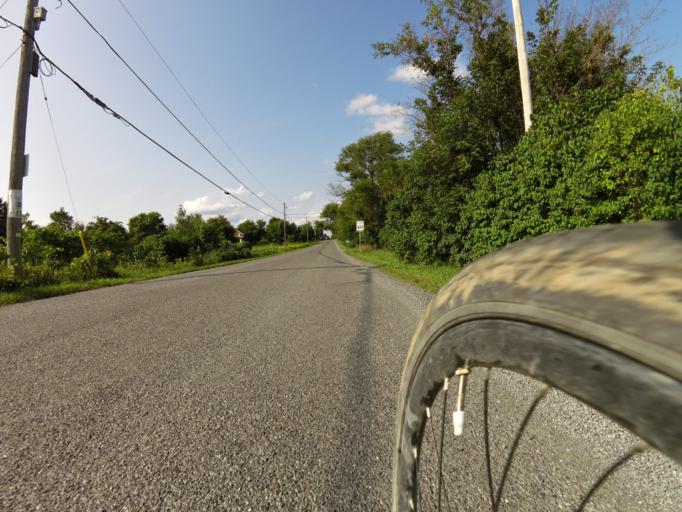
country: CA
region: Ontario
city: Kingston
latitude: 44.3819
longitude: -76.5956
